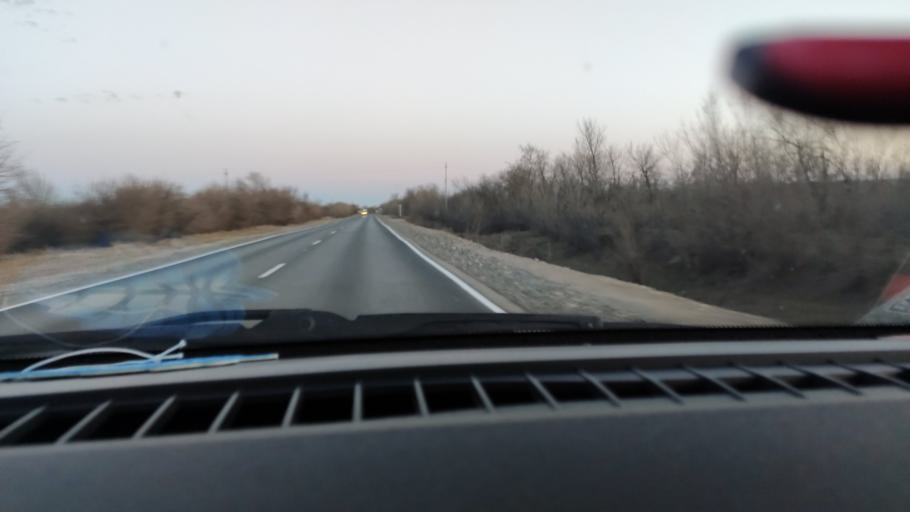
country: RU
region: Saratov
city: Krasnoarmeysk
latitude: 51.1121
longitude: 45.9578
